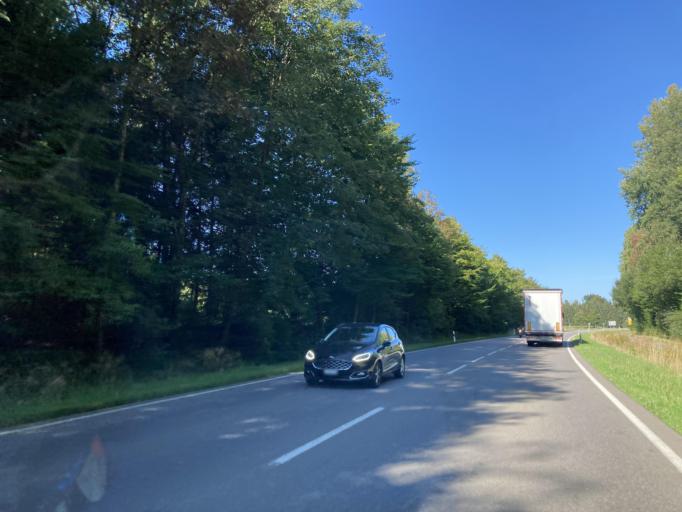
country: DE
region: Baden-Wuerttemberg
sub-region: Tuebingen Region
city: Attenweiler
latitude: 48.1154
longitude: 9.6959
